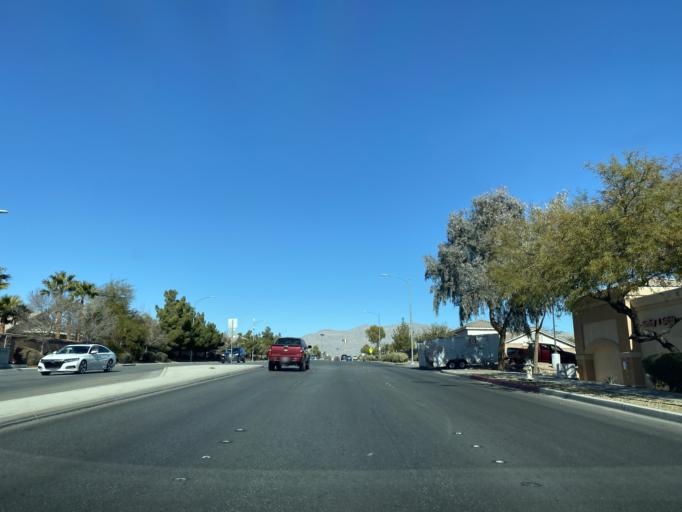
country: US
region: Nevada
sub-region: Clark County
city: North Las Vegas
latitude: 36.2630
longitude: -115.2070
